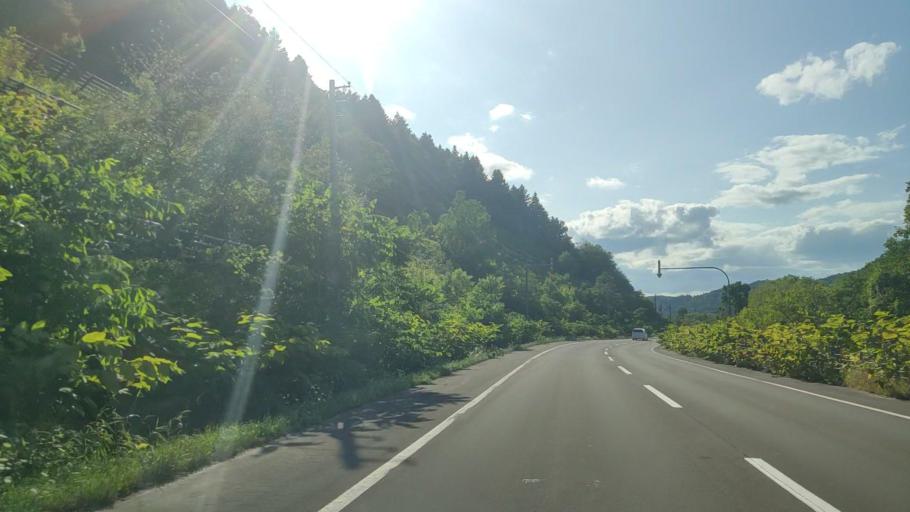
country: JP
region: Hokkaido
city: Nayoro
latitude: 44.7300
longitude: 142.0995
